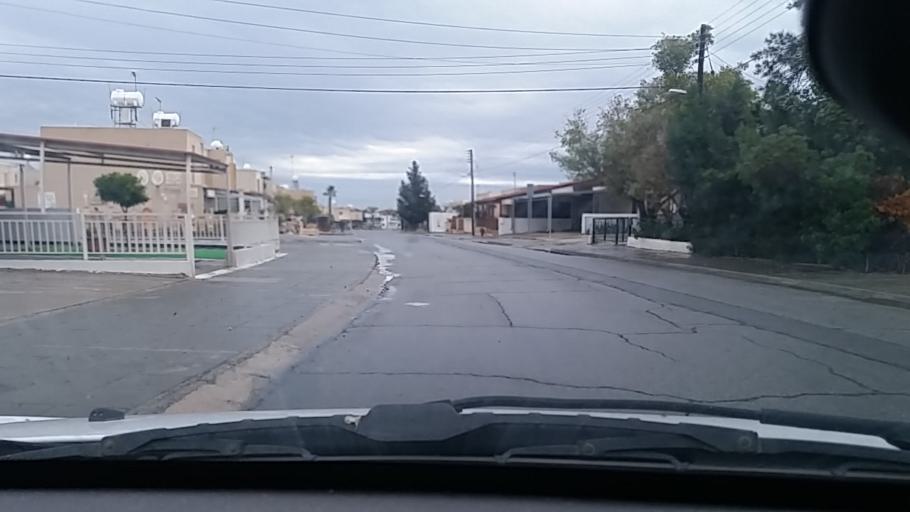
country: CY
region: Larnaka
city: Livadia
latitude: 34.9373
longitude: 33.6225
